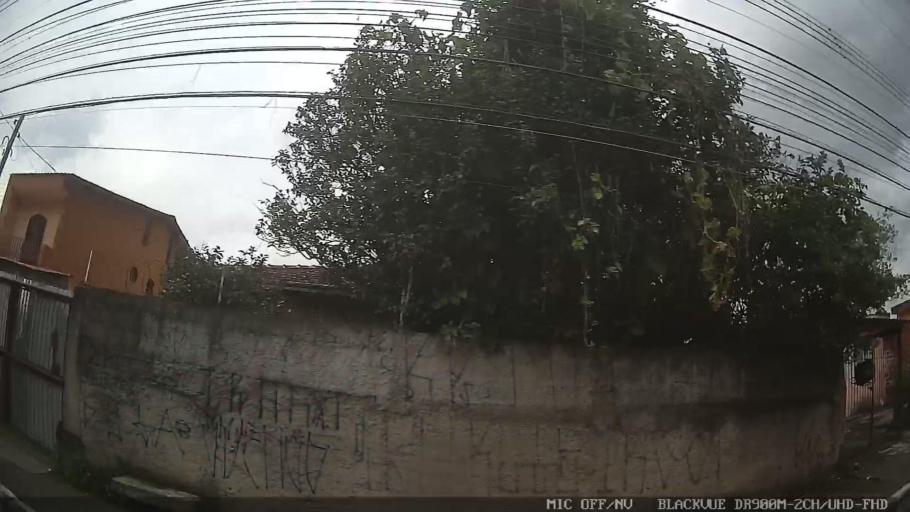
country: BR
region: Sao Paulo
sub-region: Suzano
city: Suzano
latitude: -23.5401
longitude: -46.2947
